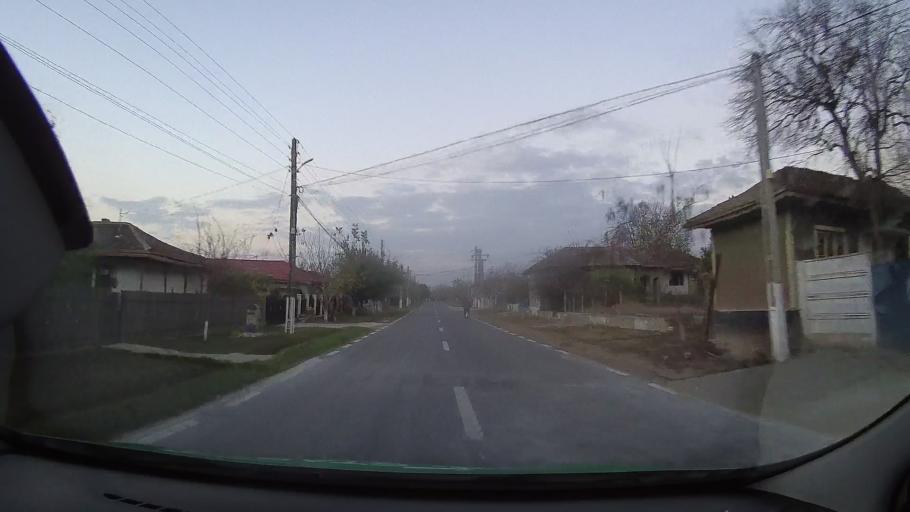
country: RO
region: Constanta
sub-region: Comuna Oltina
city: Oltina
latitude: 44.1677
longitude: 27.6664
